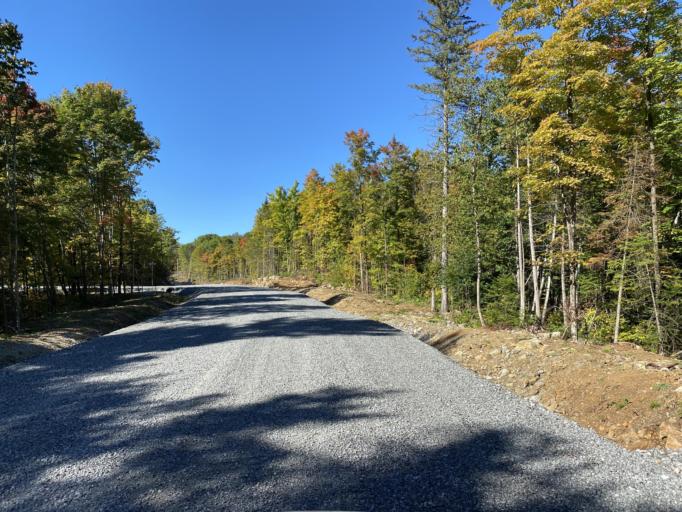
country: CA
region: Quebec
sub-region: Outaouais
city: Val-des-Monts
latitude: 45.5751
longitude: -75.5262
